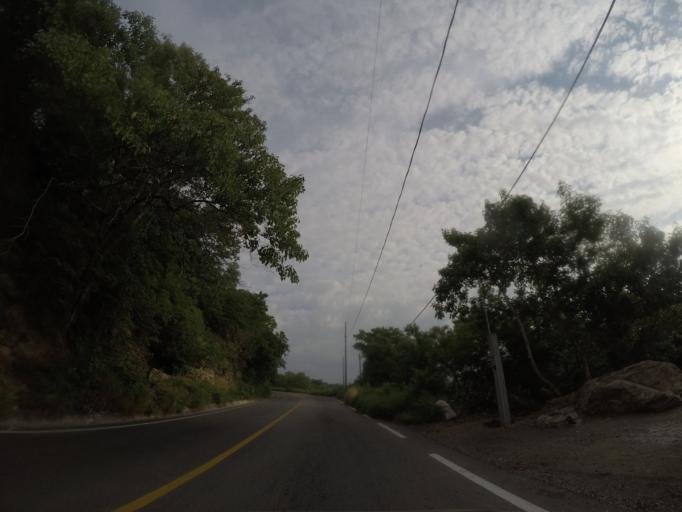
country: MX
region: Oaxaca
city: San Pedro Pochutla
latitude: 15.7045
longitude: -96.4805
